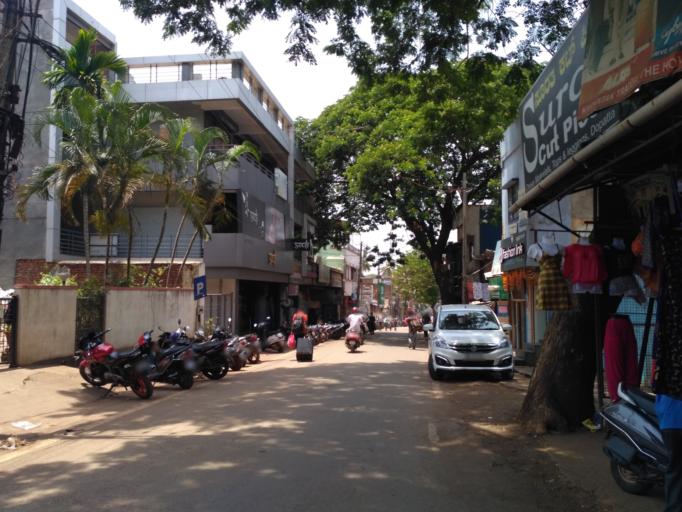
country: IN
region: Karnataka
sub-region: Dharwad
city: Hubli
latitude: 15.4567
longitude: 75.0115
